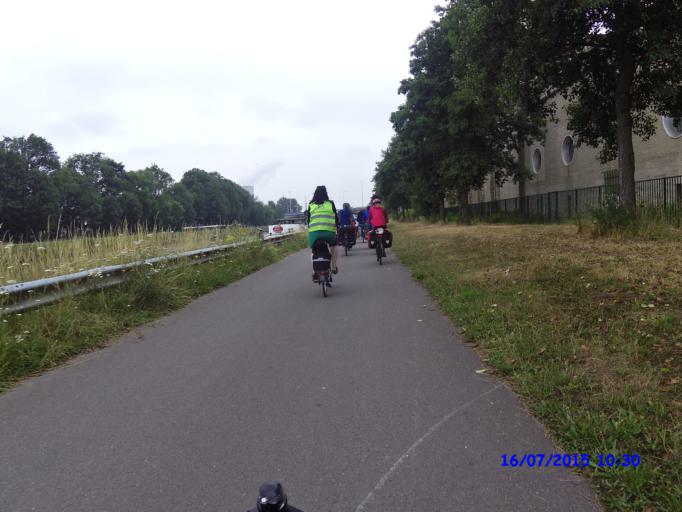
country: BE
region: Flanders
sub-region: Provincie Vlaams-Brabant
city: Drogenbos
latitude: 50.8139
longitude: 4.2987
